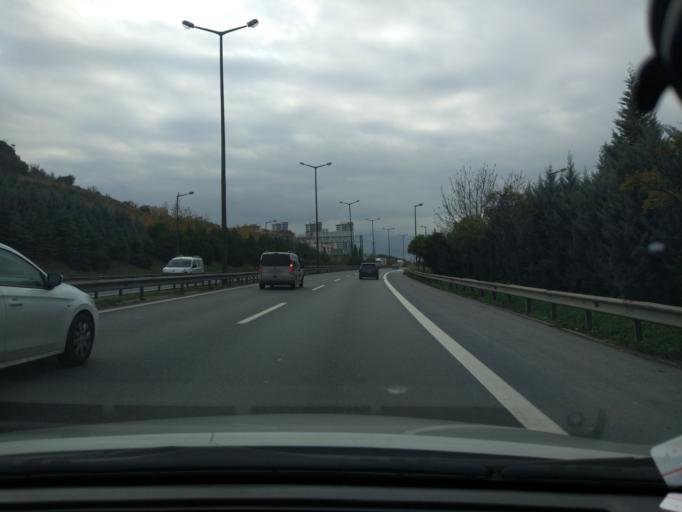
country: TR
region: Kocaeli
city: Kullar
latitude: 40.7809
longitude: 29.9776
